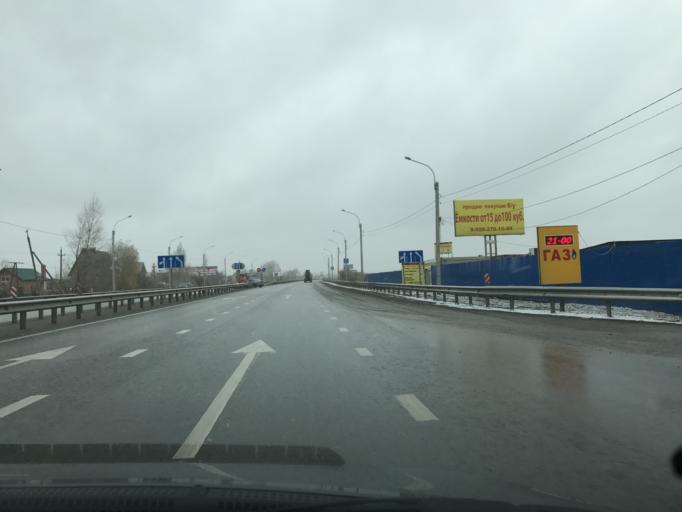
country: RU
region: Rostov
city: Bataysk
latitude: 47.1533
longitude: 39.7709
